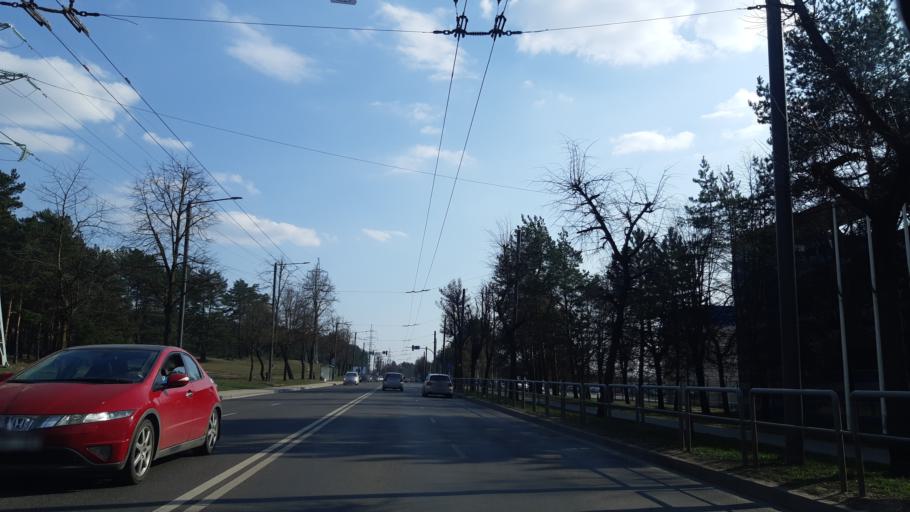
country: LT
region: Kauno apskritis
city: Dainava (Kaunas)
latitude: 54.8878
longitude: 24.0057
